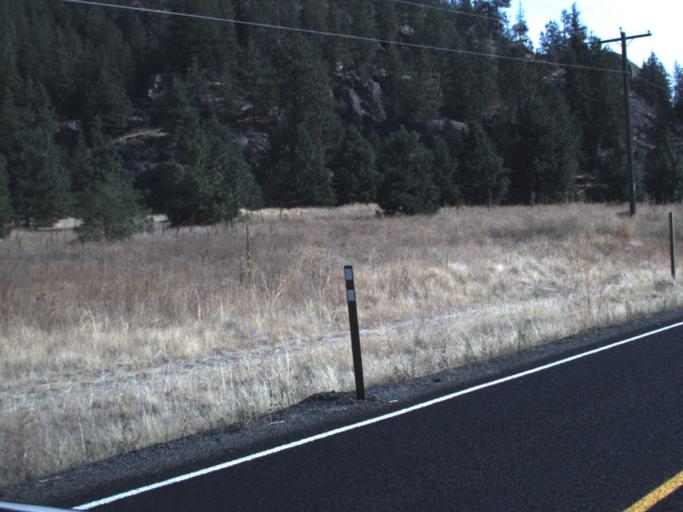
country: US
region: Washington
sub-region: Spokane County
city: Fairchild Air Force Base
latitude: 47.8387
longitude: -117.7518
